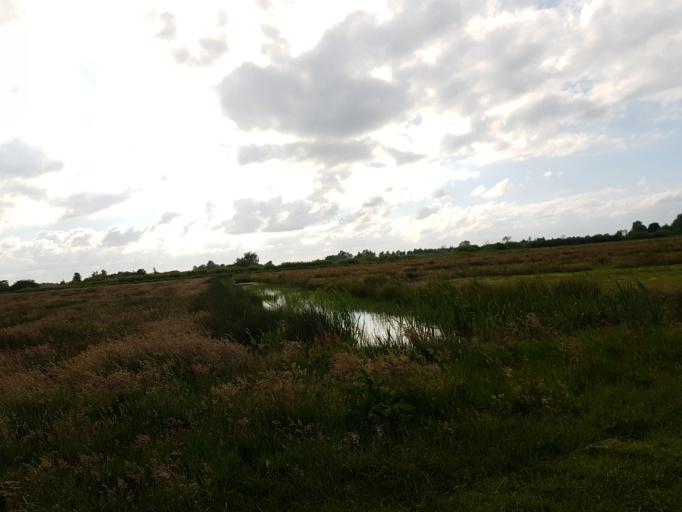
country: NL
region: Friesland
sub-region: Gemeente Smallingerland
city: Oudega
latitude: 53.0928
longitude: 5.9586
